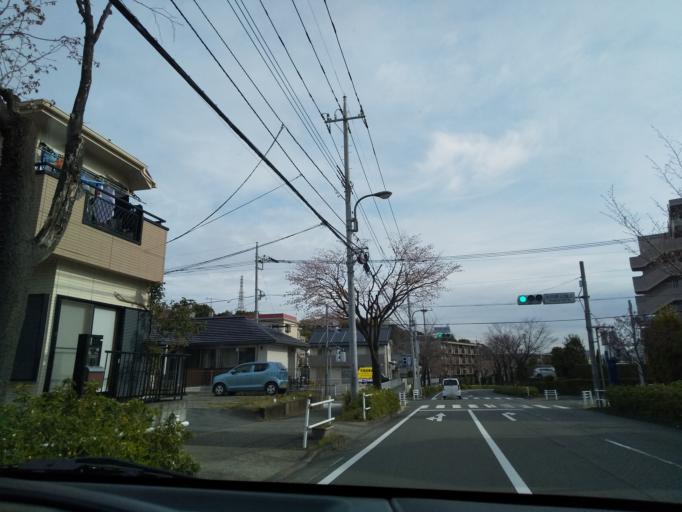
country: JP
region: Tokyo
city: Hino
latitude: 35.6156
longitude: 139.3937
